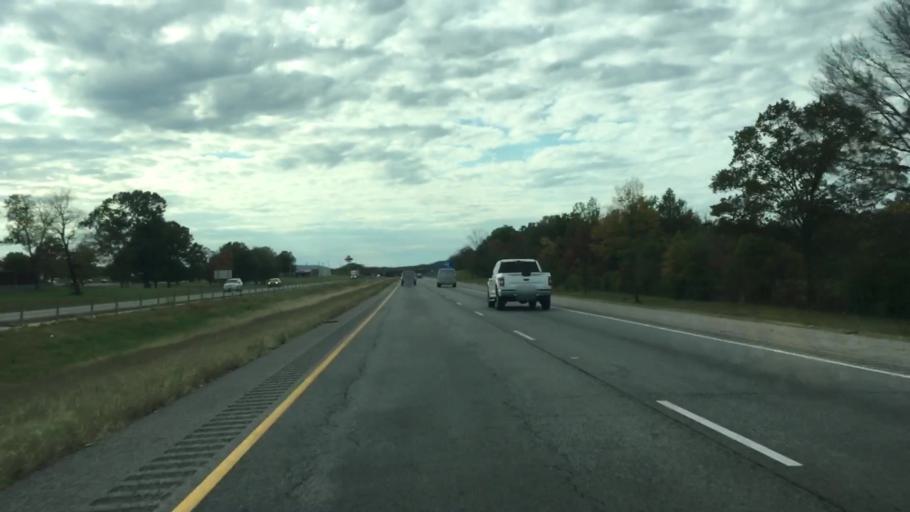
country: US
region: Arkansas
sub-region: Conway County
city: Morrilton
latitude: 35.1744
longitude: -92.7269
